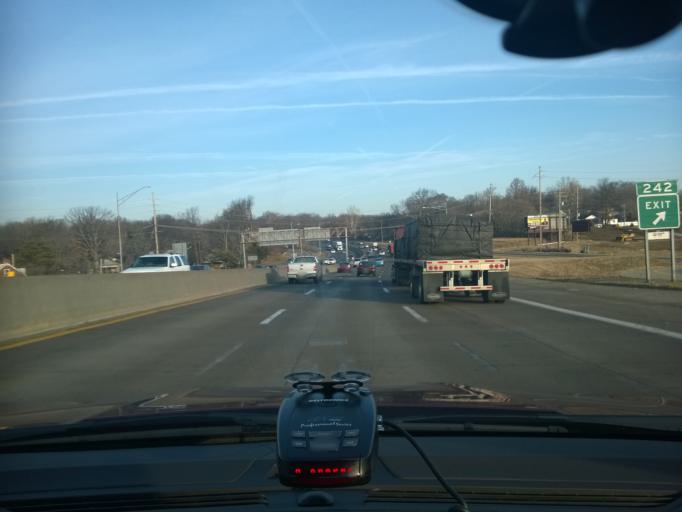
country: US
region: Missouri
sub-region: Saint Louis County
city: Pine Lawn
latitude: 38.7036
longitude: -90.2699
